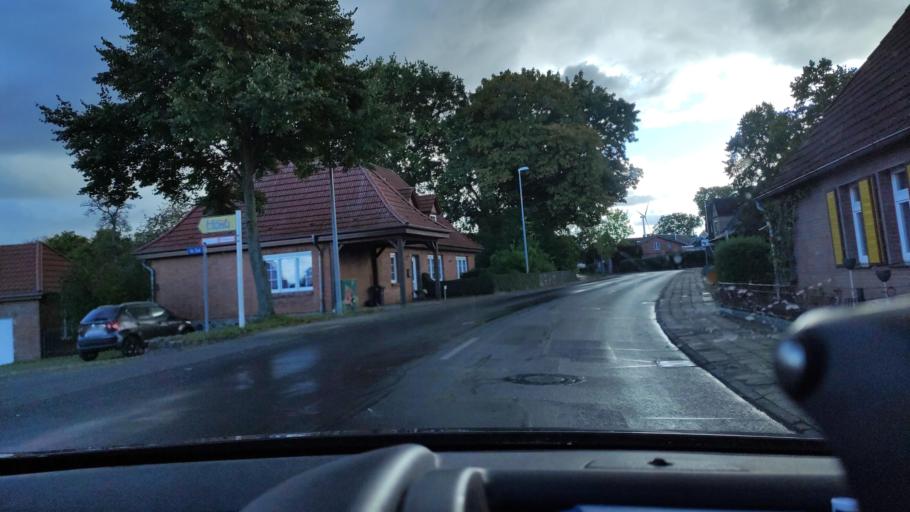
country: DE
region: Mecklenburg-Vorpommern
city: Tarnow
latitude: 53.7805
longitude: 12.0170
